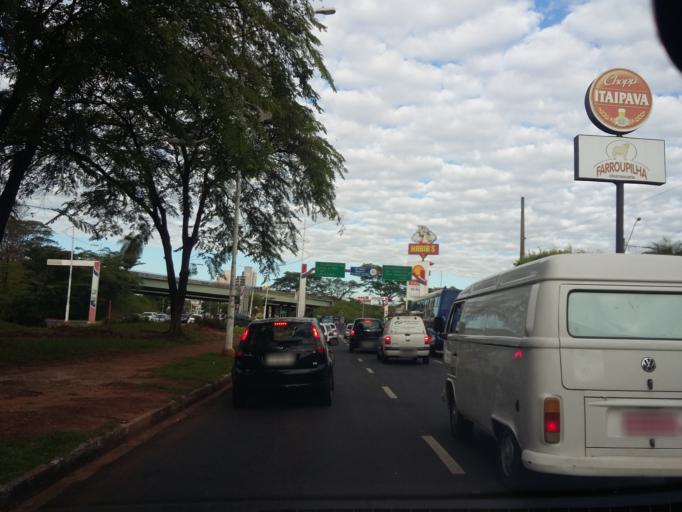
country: BR
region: Sao Paulo
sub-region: Sao Jose Do Rio Preto
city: Sao Jose do Rio Preto
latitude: -20.8236
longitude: -49.4019
